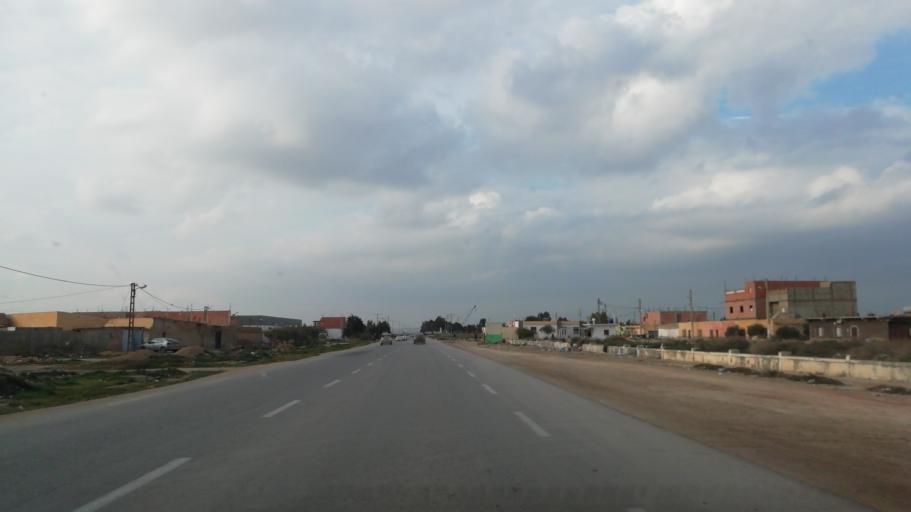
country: DZ
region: Mascara
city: Sig
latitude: 35.6907
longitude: -0.0179
